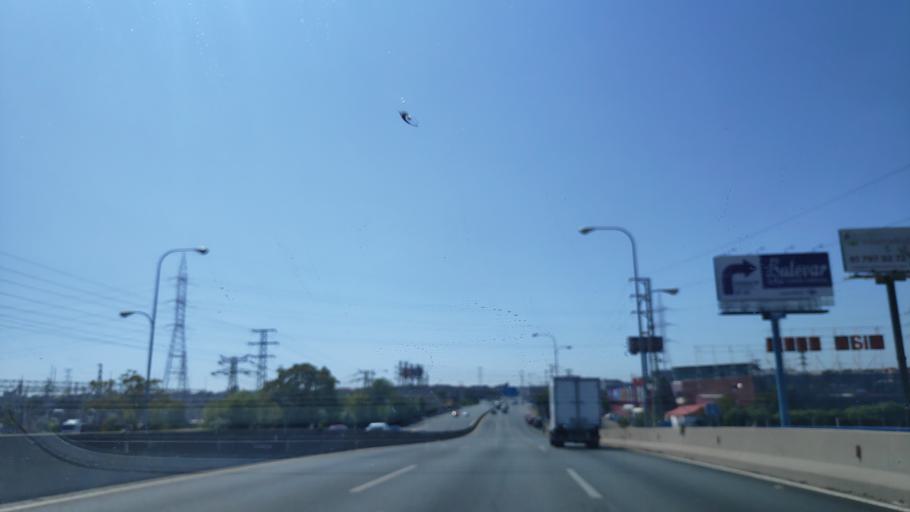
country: ES
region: Madrid
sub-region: Provincia de Madrid
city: Villaverde
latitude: 40.3375
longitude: -3.7246
